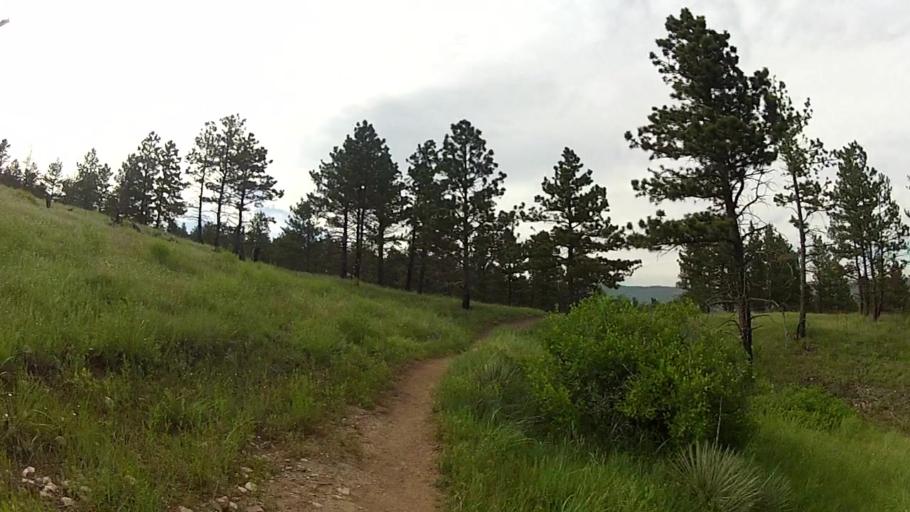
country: US
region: Colorado
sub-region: Larimer County
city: Laporte
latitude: 40.4780
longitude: -105.2355
